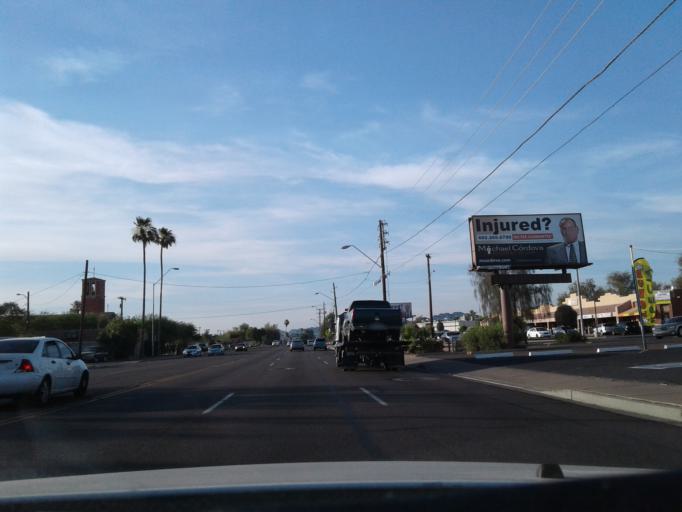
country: US
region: Arizona
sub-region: Maricopa County
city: Phoenix
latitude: 33.4667
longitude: -112.0301
